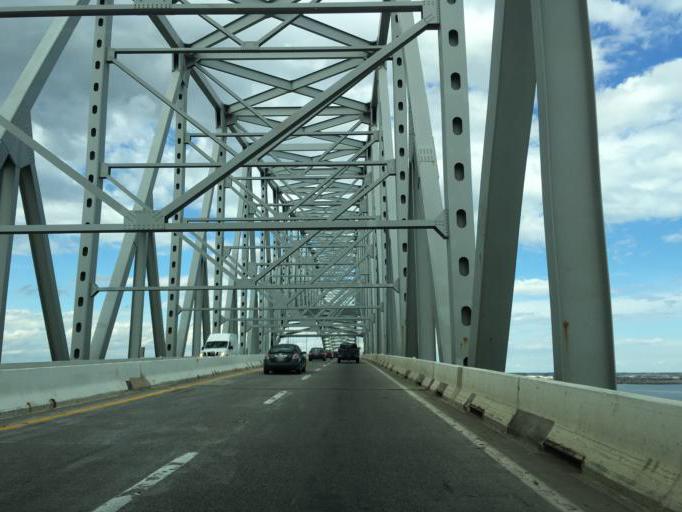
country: US
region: Maryland
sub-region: Baltimore County
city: Dundalk
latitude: 39.2151
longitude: -76.5306
